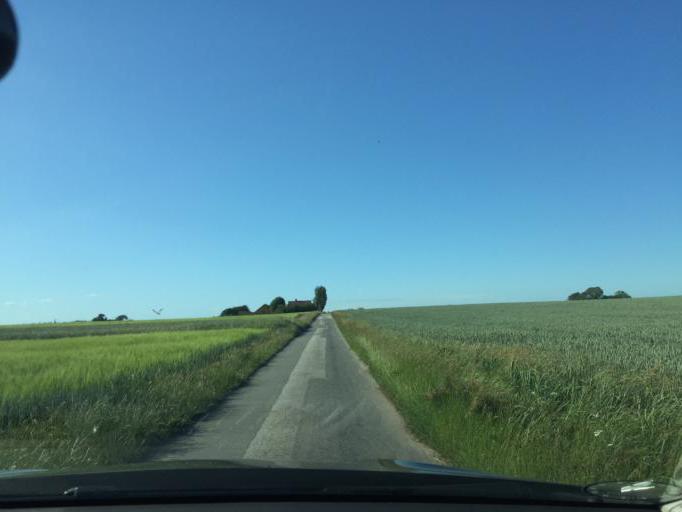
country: DK
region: Zealand
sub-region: Slagelse Kommune
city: Skaelskor
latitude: 55.2004
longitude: 11.1819
